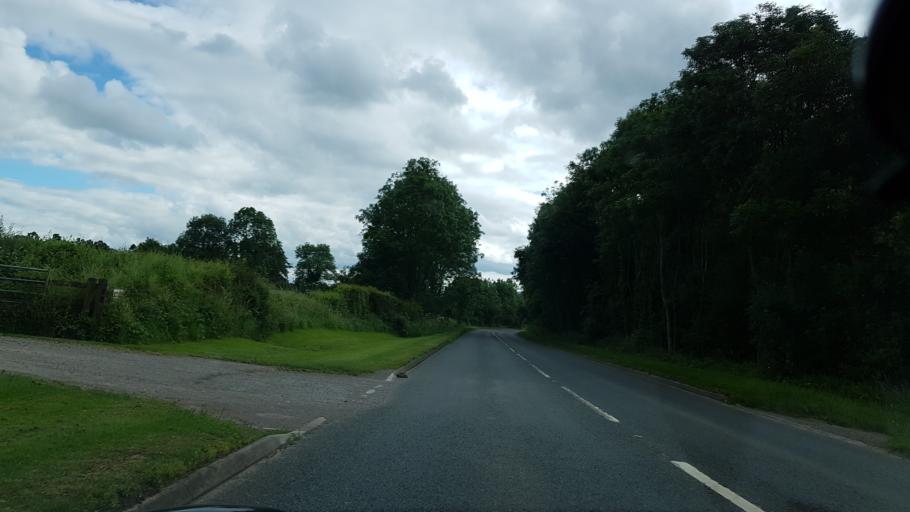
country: GB
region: Wales
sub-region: Monmouthshire
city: Abergavenny
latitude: 51.8581
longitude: -2.9987
